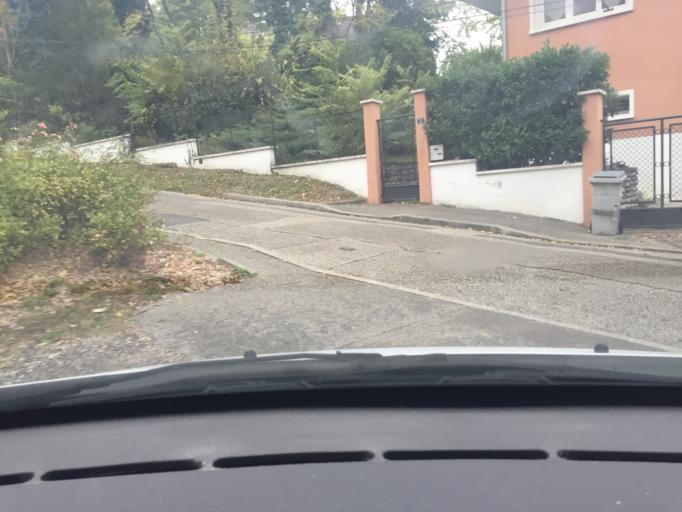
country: FR
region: Rhone-Alpes
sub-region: Departement du Rhone
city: Rillieux-la-Pape
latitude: 45.8036
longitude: 4.8808
